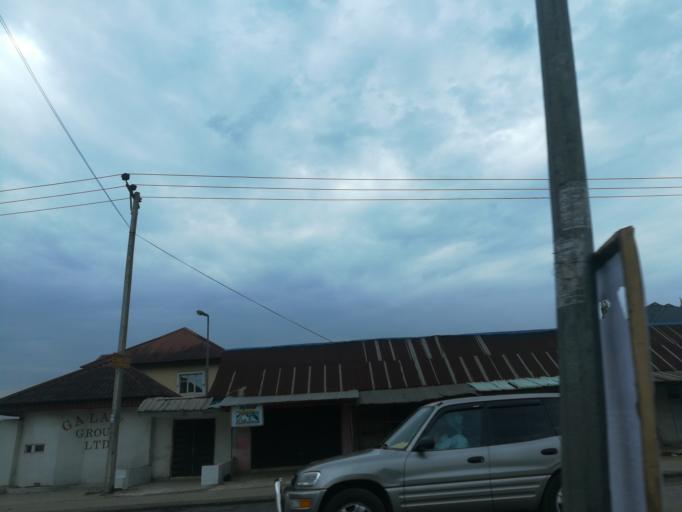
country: NG
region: Rivers
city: Port Harcourt
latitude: 4.8139
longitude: 6.9488
